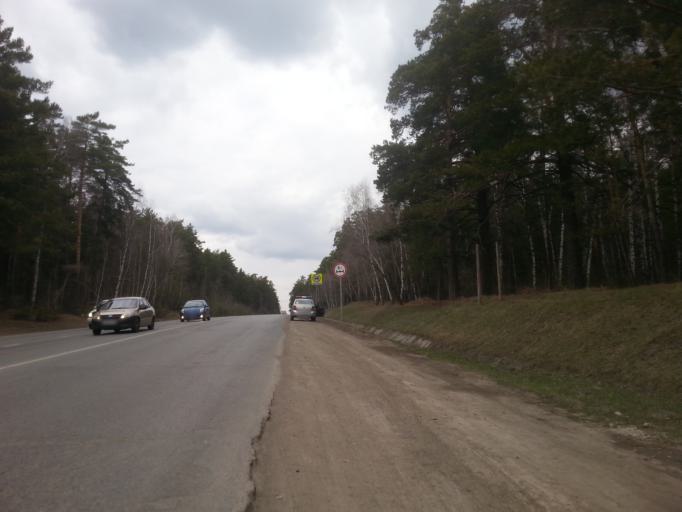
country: RU
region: Altai Krai
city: Yuzhnyy
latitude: 53.2689
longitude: 83.7260
